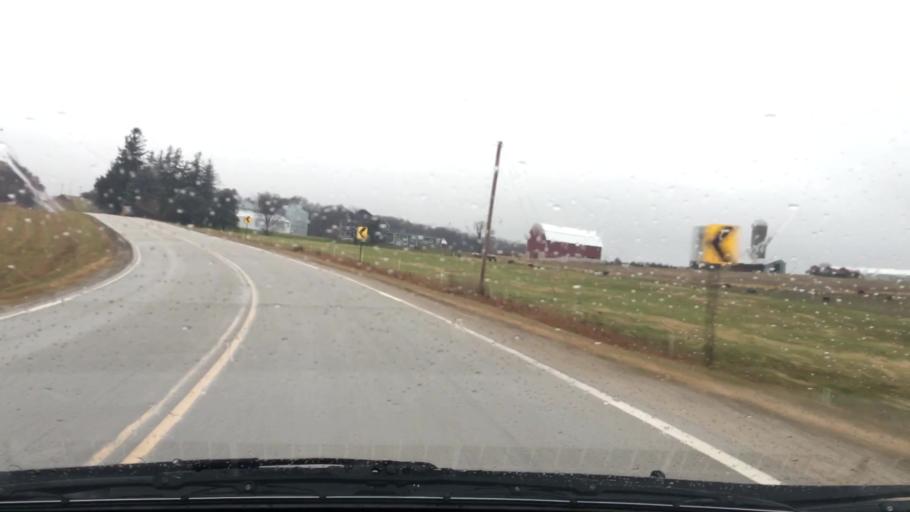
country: US
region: Minnesota
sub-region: Fillmore County
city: Preston
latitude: 43.7328
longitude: -92.0008
